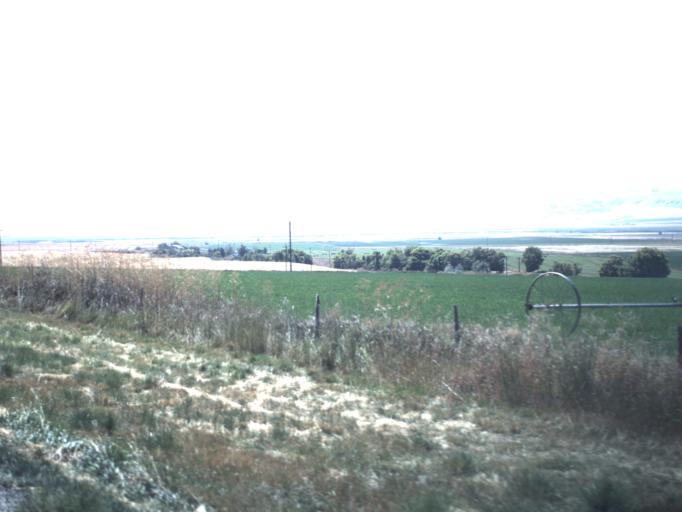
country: US
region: Utah
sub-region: Cache County
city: Benson
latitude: 41.8544
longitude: -111.9731
